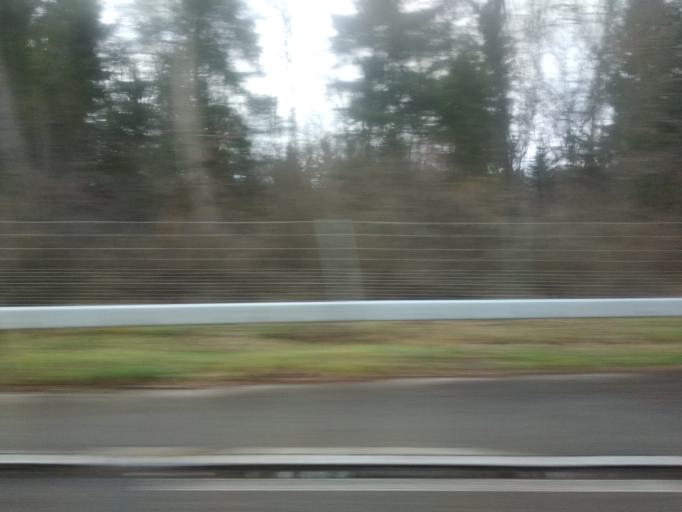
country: CH
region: Saint Gallen
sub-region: Wahlkreis Wil
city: Uzwil
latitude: 47.4535
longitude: 9.1393
